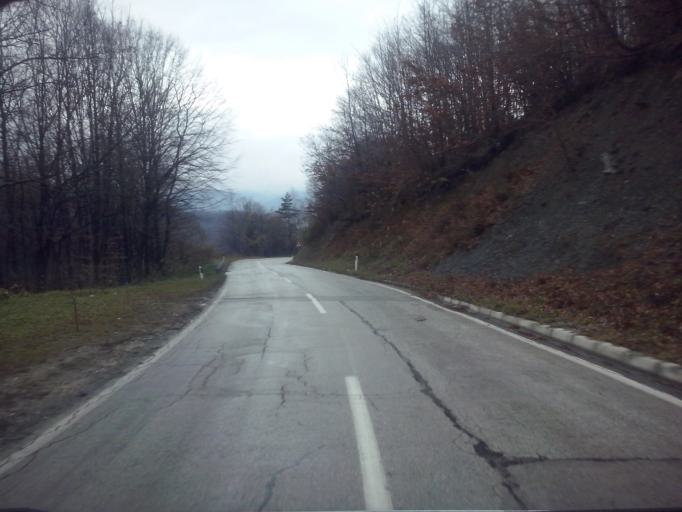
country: RS
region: Central Serbia
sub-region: Moravicki Okrug
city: Ivanjica
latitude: 43.5354
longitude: 20.2828
